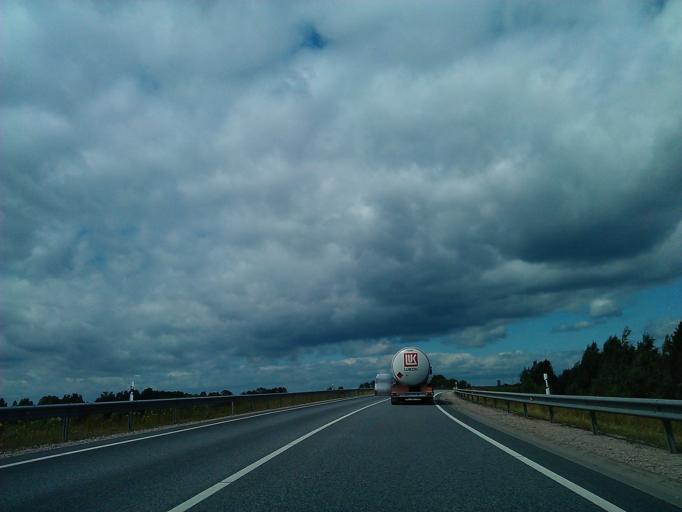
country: LV
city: Tireli
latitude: 56.9284
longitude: 23.6220
